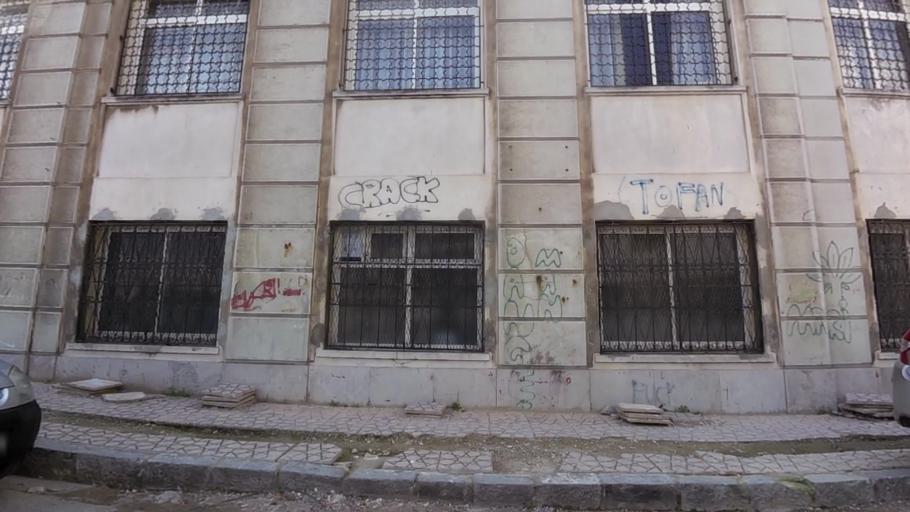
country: MA
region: Tanger-Tetouan
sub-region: Tanger-Assilah
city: Tangier
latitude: 35.7815
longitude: -5.8106
